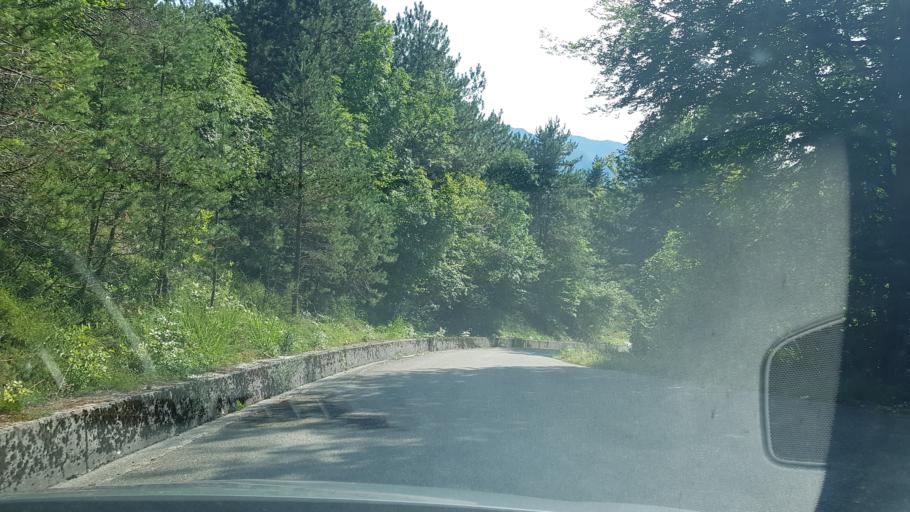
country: IT
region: Friuli Venezia Giulia
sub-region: Provincia di Udine
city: Moggio Udinese
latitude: 46.4392
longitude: 13.2052
